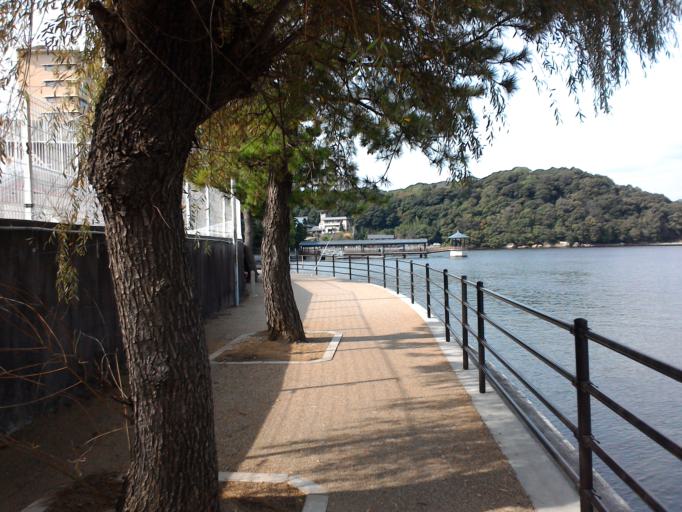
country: JP
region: Shizuoka
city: Kosai-shi
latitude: 34.7661
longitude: 137.6168
